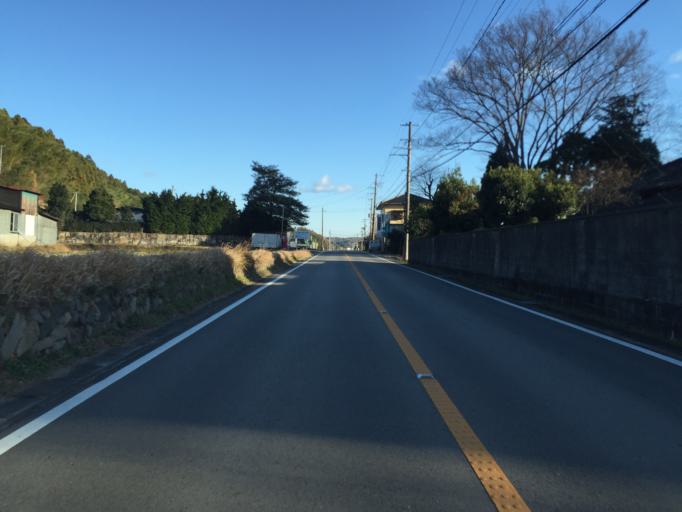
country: JP
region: Fukushima
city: Iwaki
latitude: 37.1413
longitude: 140.8417
